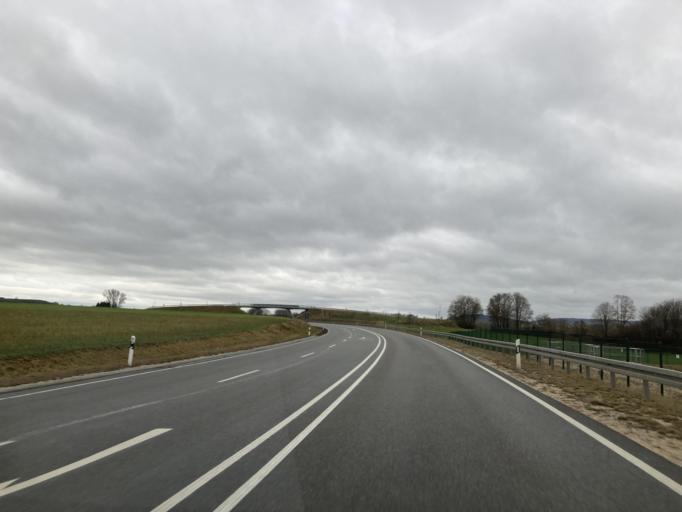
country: DE
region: Baden-Wuerttemberg
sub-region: Tuebingen Region
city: Unlingen
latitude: 48.1818
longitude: 9.5179
